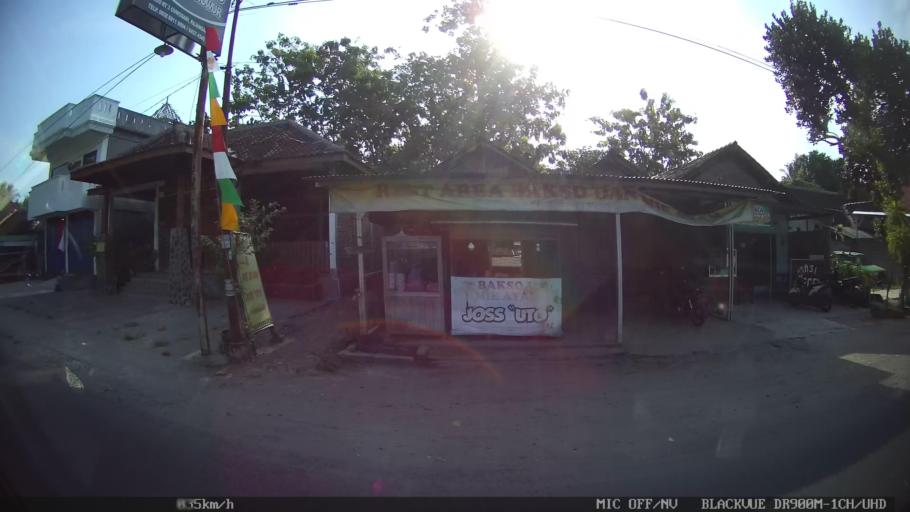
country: ID
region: Daerah Istimewa Yogyakarta
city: Pandak
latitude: -7.8897
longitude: 110.3035
